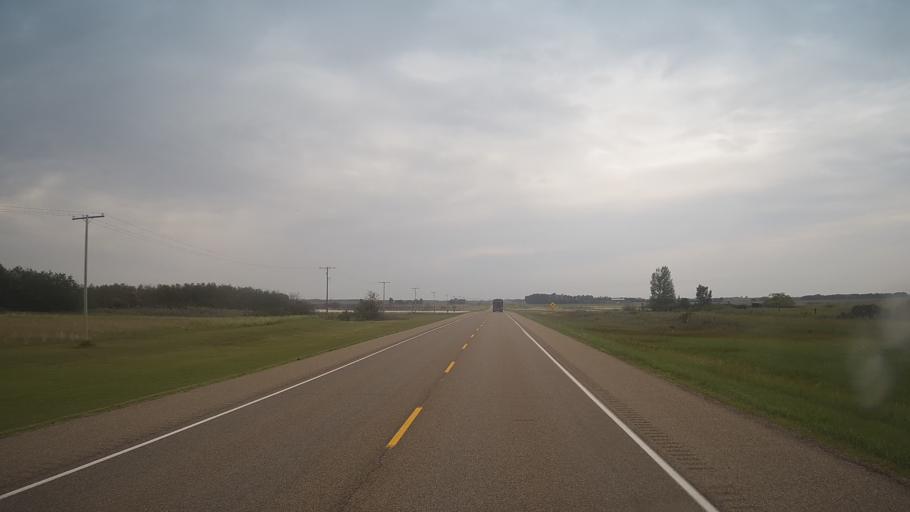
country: CA
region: Saskatchewan
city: Langham
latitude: 52.1289
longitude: -107.1228
